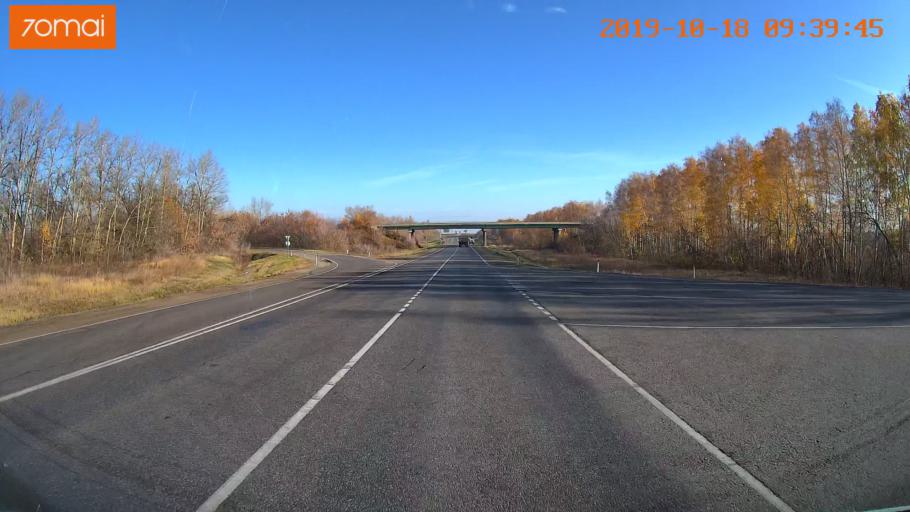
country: RU
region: Tula
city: Yefremov
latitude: 53.2567
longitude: 38.1391
